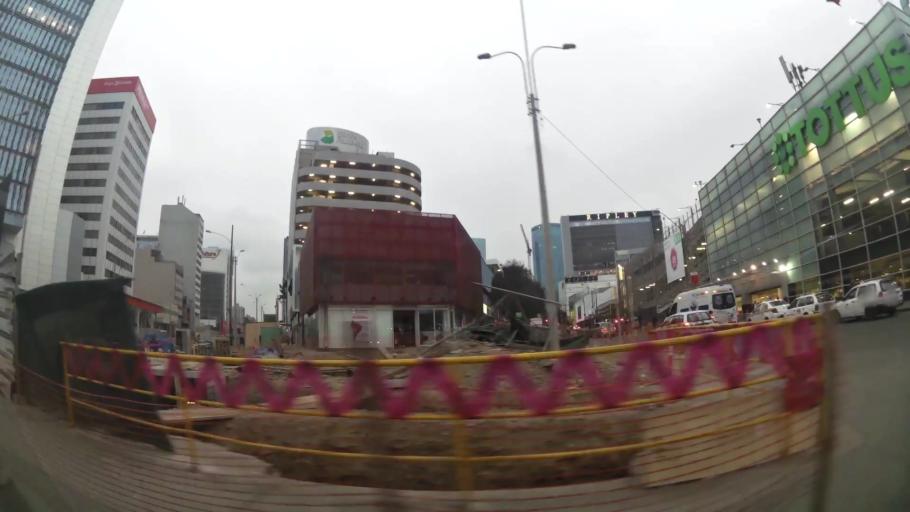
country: PE
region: Lima
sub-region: Lima
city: San Isidro
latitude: -12.0964
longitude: -77.0261
